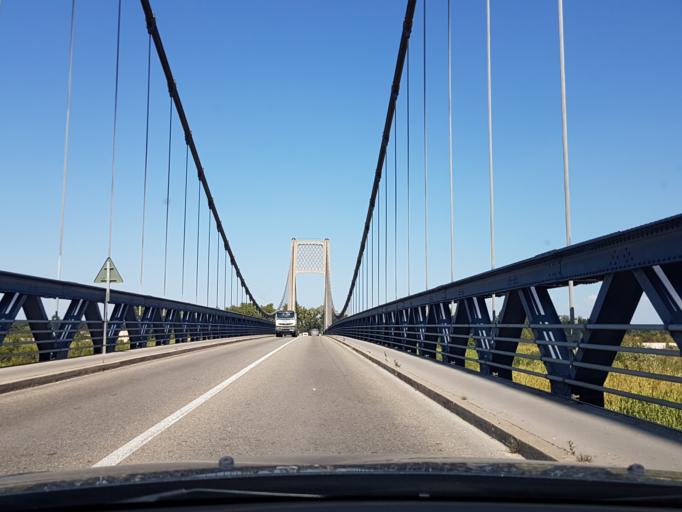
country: FR
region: Provence-Alpes-Cote d'Azur
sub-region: Departement des Bouches-du-Rhone
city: Rognonas
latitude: 43.9139
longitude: 4.8078
